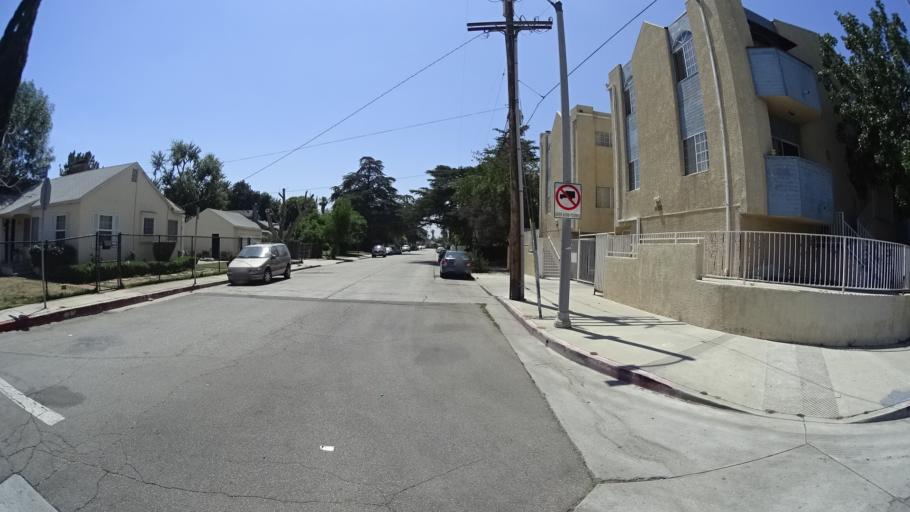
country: US
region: California
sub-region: Los Angeles County
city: Van Nuys
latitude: 34.1919
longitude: -118.4401
